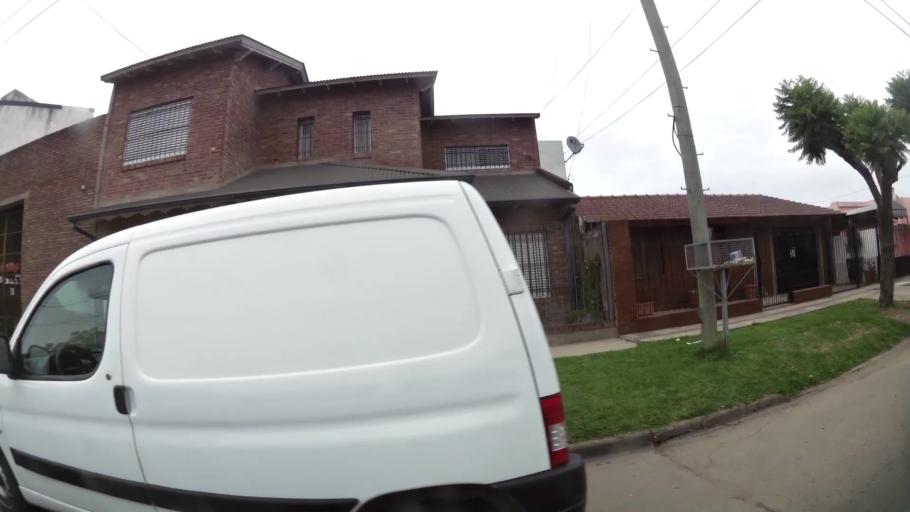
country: AR
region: Buenos Aires
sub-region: Partido de Zarate
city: Zarate
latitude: -34.1091
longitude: -59.0238
